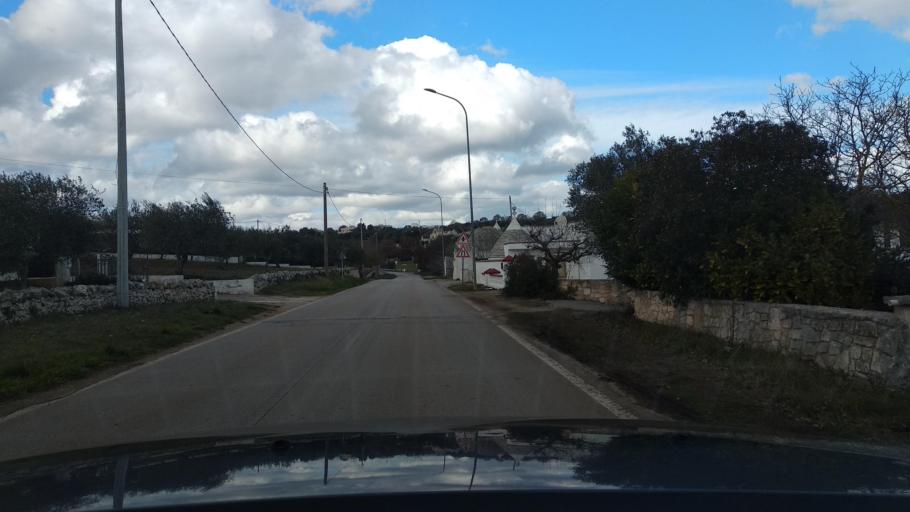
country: IT
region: Apulia
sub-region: Provincia di Brindisi
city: Cisternino
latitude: 40.7654
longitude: 17.3934
